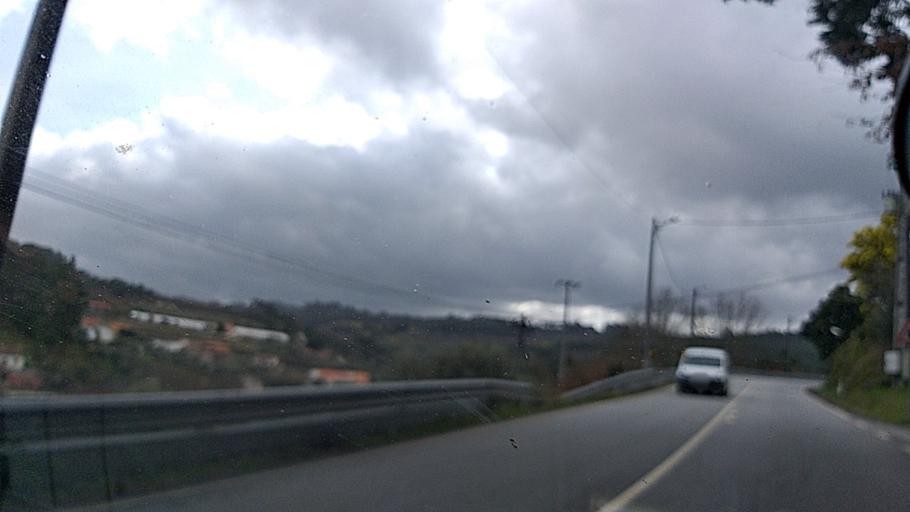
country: PT
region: Viseu
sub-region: Mangualde
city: Mangualde
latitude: 40.6359
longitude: -7.7402
